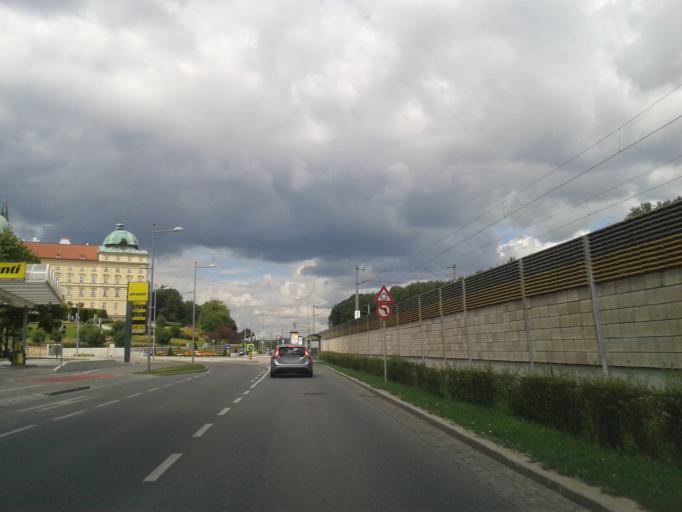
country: AT
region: Lower Austria
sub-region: Politischer Bezirk Wien-Umgebung
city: Klosterneuburg
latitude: 48.3042
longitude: 16.3304
